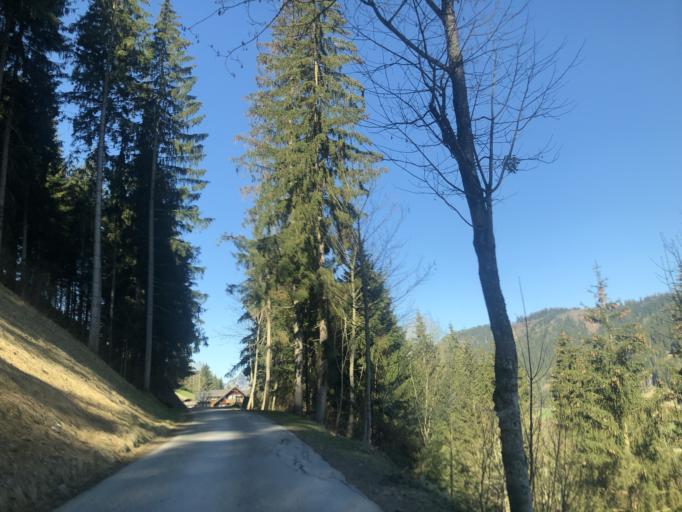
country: AT
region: Styria
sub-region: Politischer Bezirk Liezen
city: Schladming
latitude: 47.3864
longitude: 13.6552
